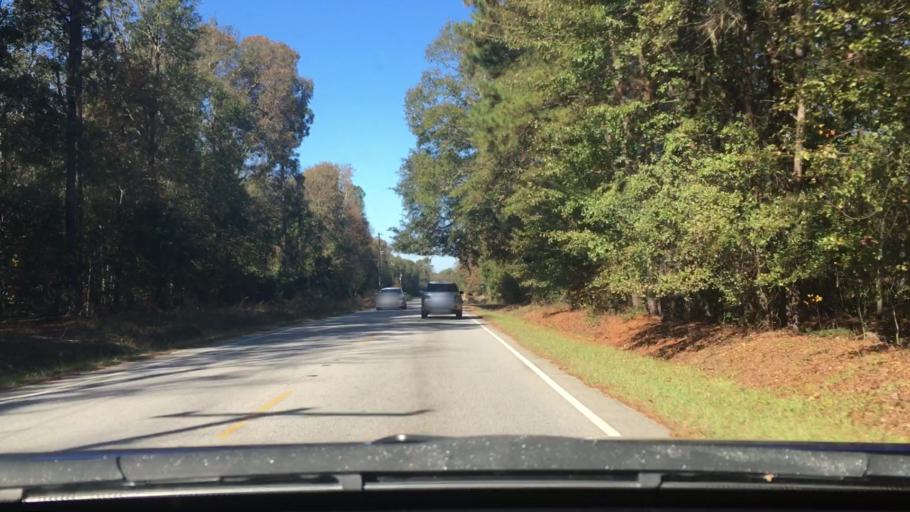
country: US
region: South Carolina
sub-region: Sumter County
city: Lakewood
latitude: 33.8701
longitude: -80.3620
